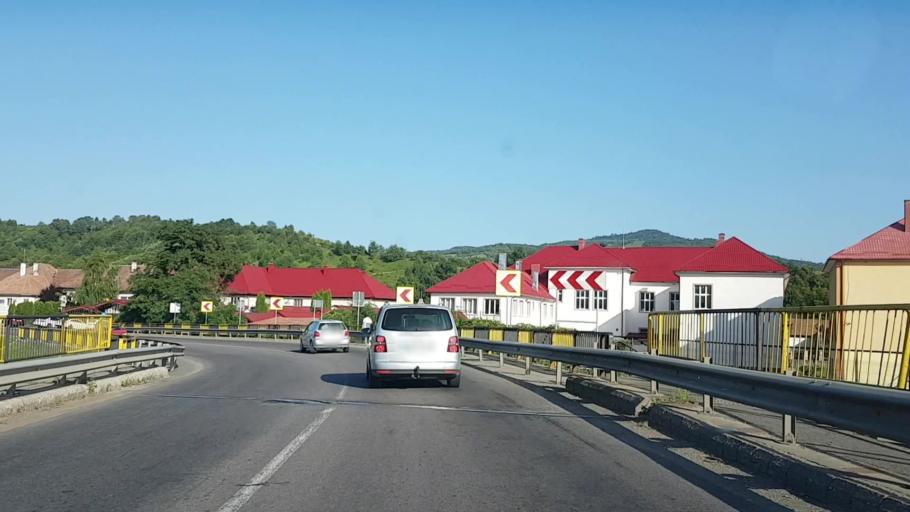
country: RO
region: Bistrita-Nasaud
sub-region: Comuna Josenii Bargaului
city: Josenii Bargaului
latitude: 47.2120
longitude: 24.6770
